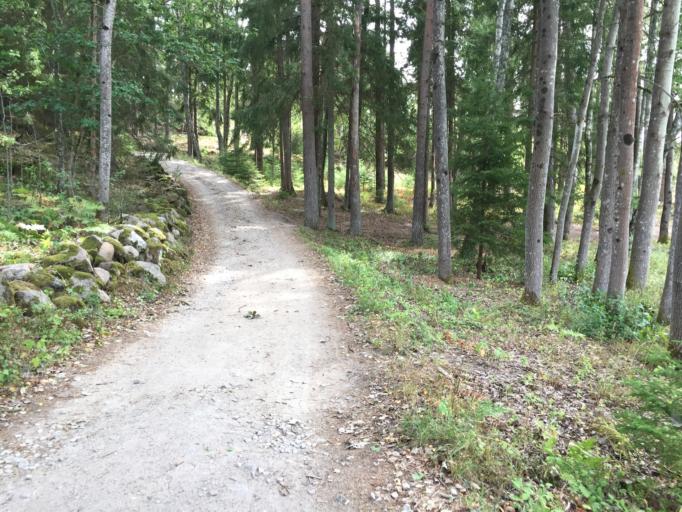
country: NO
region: Ostfold
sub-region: Fredrikstad
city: Fredrikstad
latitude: 59.0987
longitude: 10.9265
